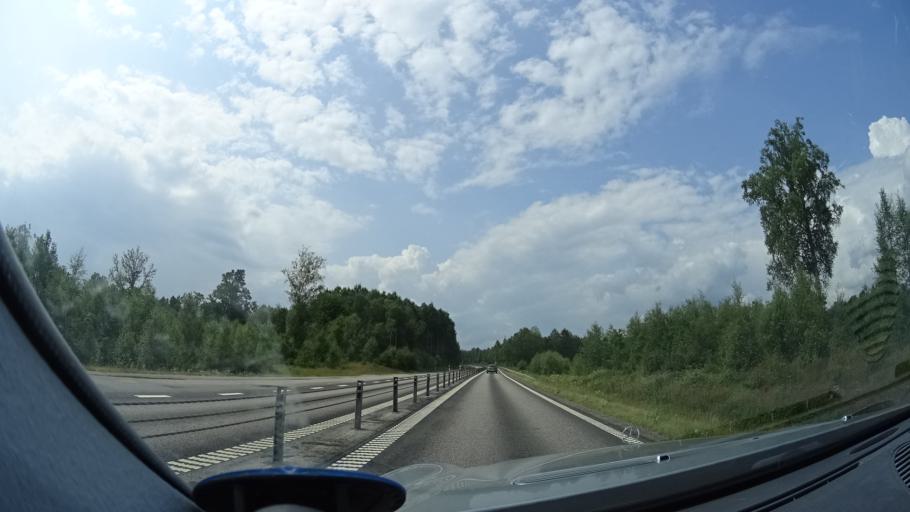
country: SE
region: Kalmar
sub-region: Nybro Kommun
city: Nybro
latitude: 56.7338
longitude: 15.8586
